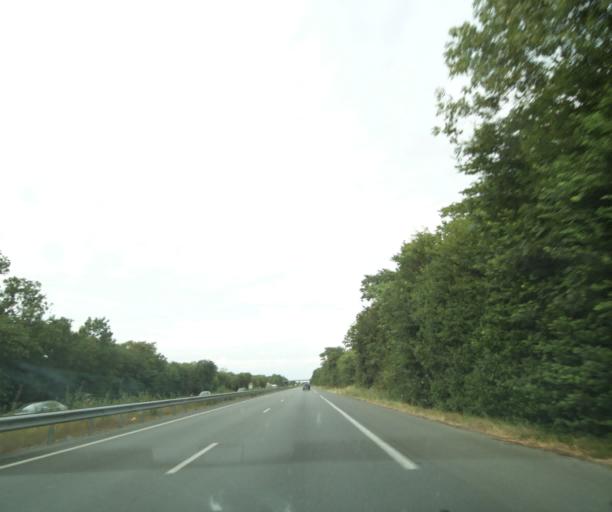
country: FR
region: Poitou-Charentes
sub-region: Departement de la Charente-Maritime
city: Dompierre-sur-Mer
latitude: 46.1868
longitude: -1.0755
